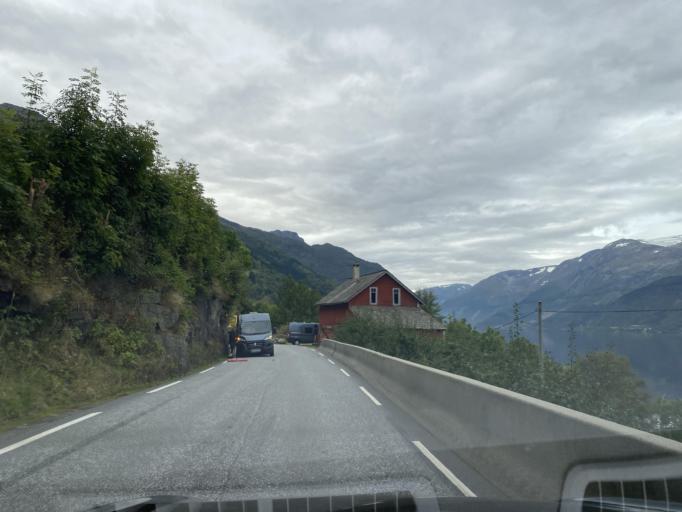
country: NO
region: Hordaland
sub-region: Odda
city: Odda
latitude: 60.2172
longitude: 6.6026
